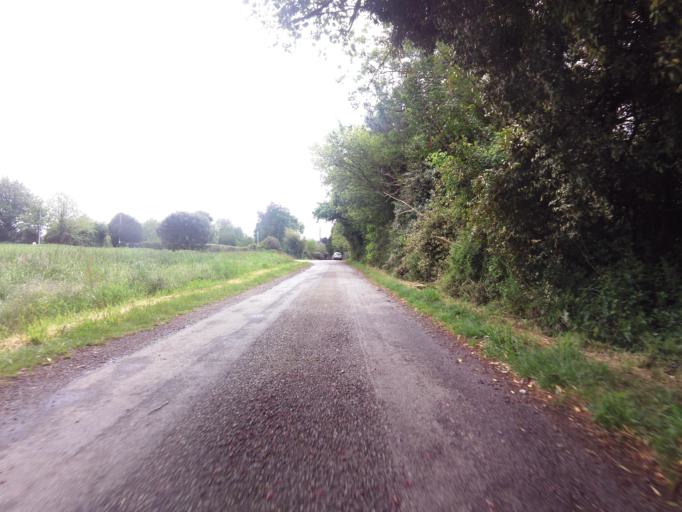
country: FR
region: Brittany
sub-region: Departement du Morbihan
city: Baden
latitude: 47.6044
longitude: -2.9288
